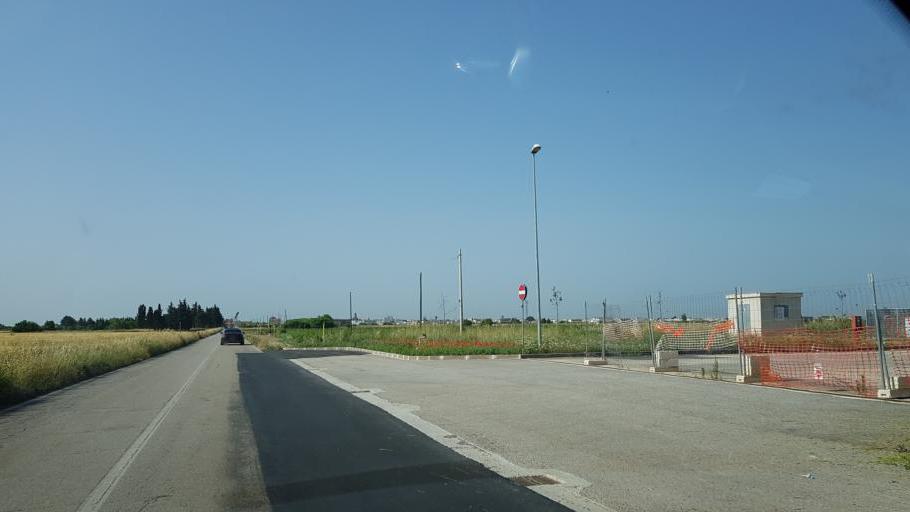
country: IT
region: Apulia
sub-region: Provincia di Brindisi
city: San Pancrazio Salentino
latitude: 40.4313
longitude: 17.8401
